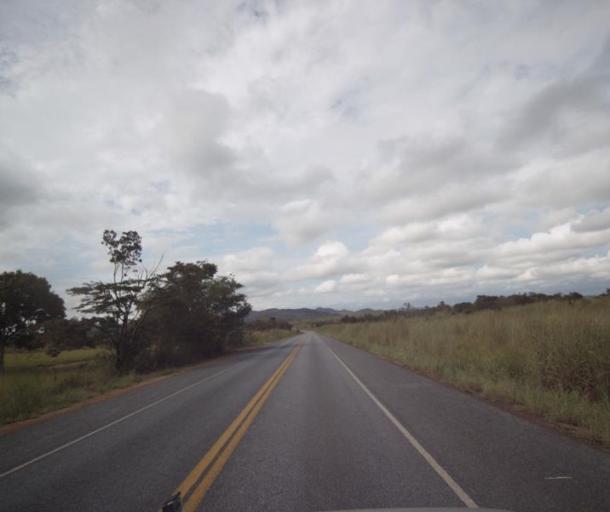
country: BR
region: Goias
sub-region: Pirenopolis
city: Pirenopolis
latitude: -15.5519
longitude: -48.6230
